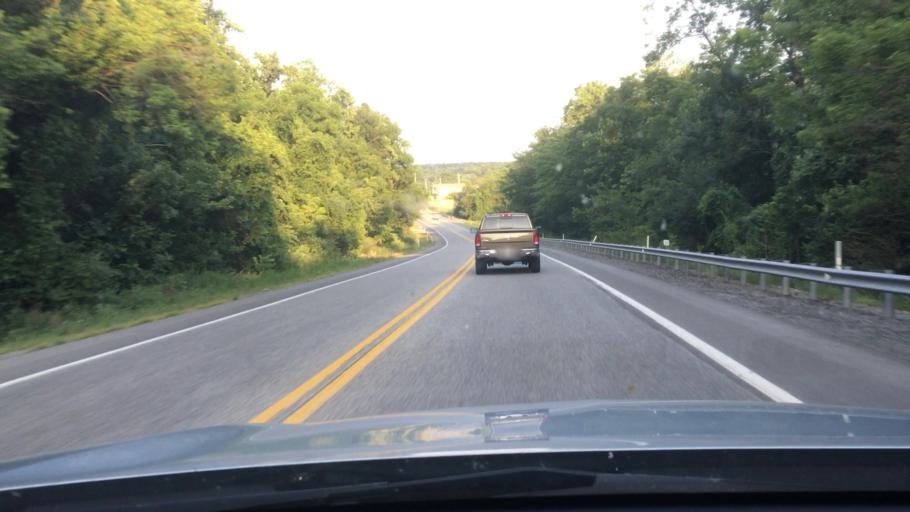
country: US
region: Pennsylvania
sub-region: York County
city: Dillsburg
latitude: 40.0826
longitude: -76.9392
